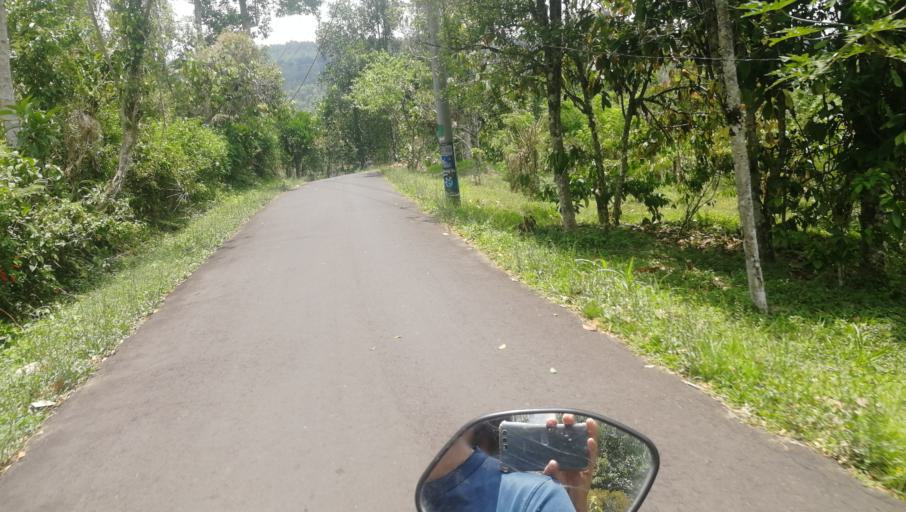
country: ID
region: Bali
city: Munduk
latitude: -8.2902
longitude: 115.0431
